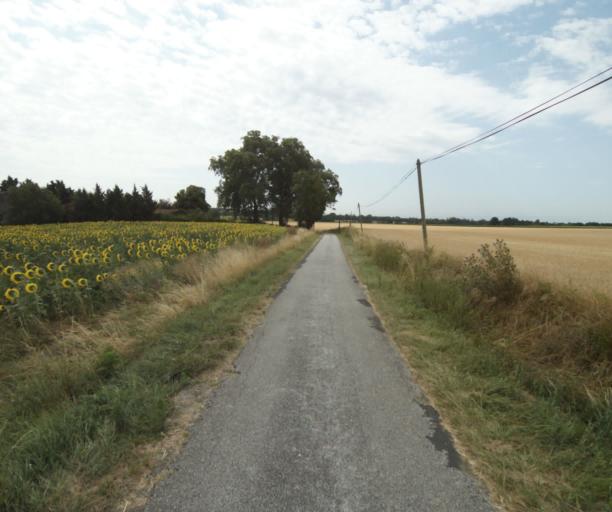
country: FR
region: Midi-Pyrenees
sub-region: Departement de la Haute-Garonne
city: Saint-Felix-Lauragais
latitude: 43.4424
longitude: 1.9092
